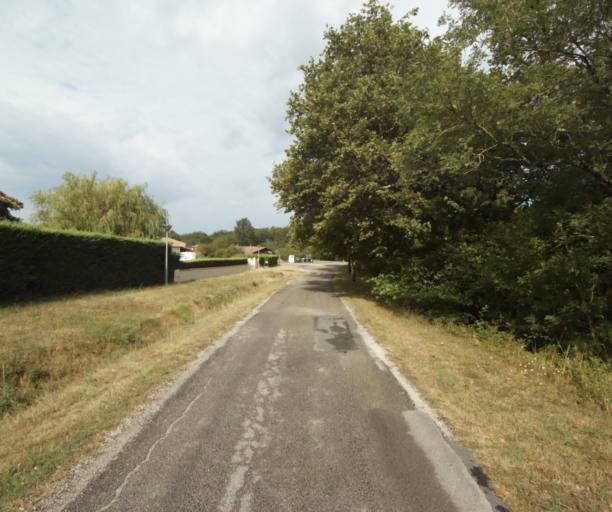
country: FR
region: Midi-Pyrenees
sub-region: Departement de la Haute-Garonne
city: Revel
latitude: 43.4278
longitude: 1.9869
